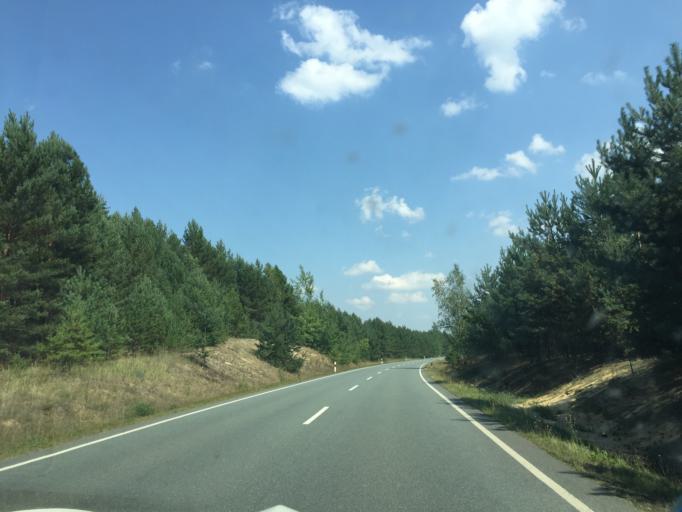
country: DE
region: Saxony
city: Uhyst
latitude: 51.3893
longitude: 14.4990
